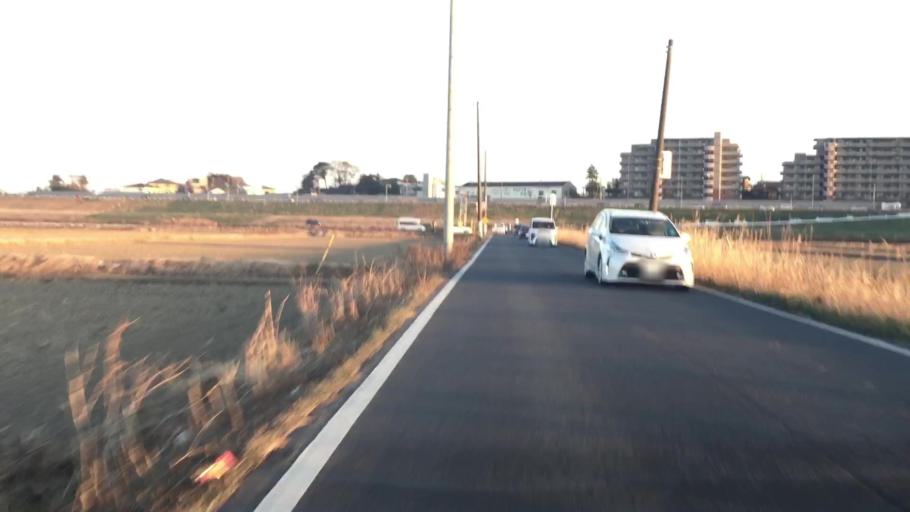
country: JP
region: Chiba
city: Abiko
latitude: 35.8836
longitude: 140.0418
